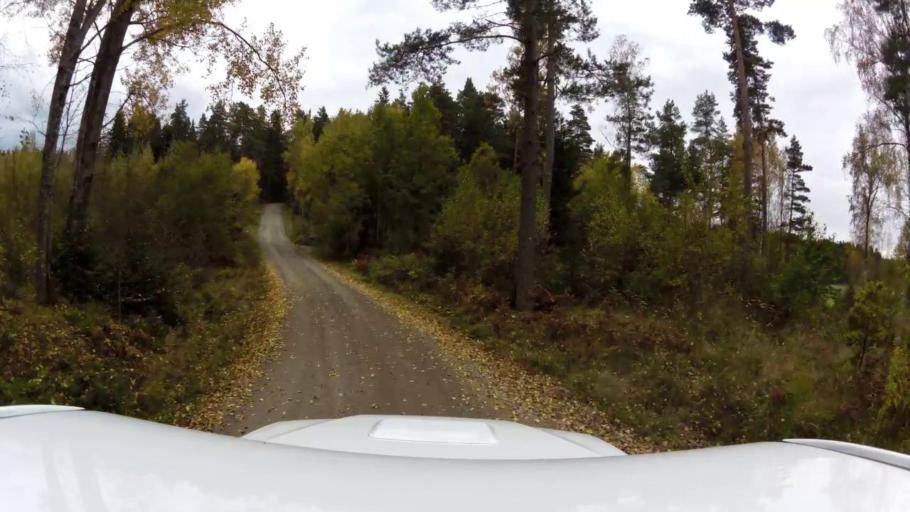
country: SE
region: OEstergoetland
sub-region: Linkopings Kommun
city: Ljungsbro
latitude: 58.5532
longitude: 15.4246
